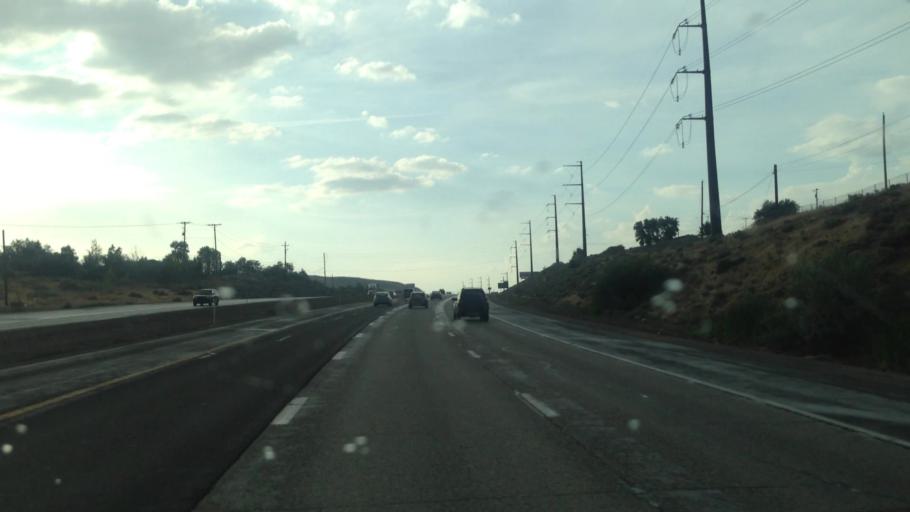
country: US
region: Nevada
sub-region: Washoe County
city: Golden Valley
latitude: 39.5812
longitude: -119.8182
